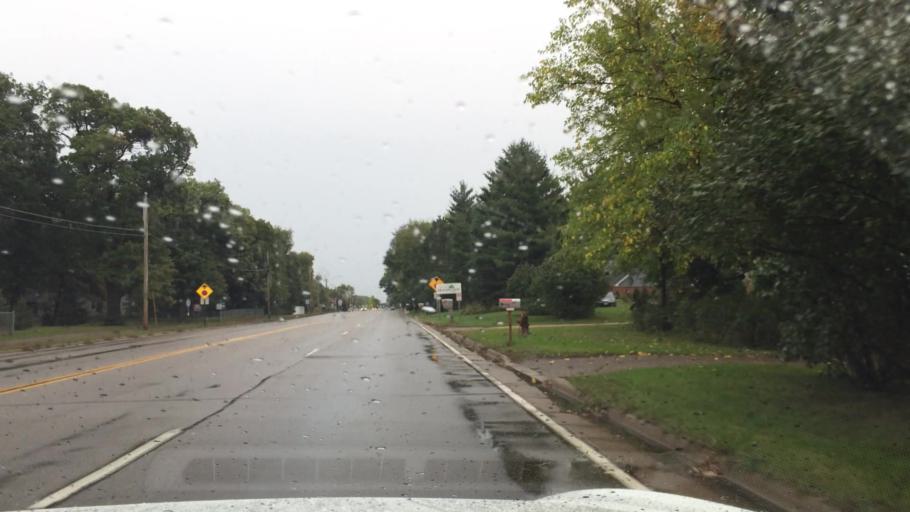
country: US
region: Minnesota
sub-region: Anoka County
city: Spring Lake Park
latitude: 45.1245
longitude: -93.2281
